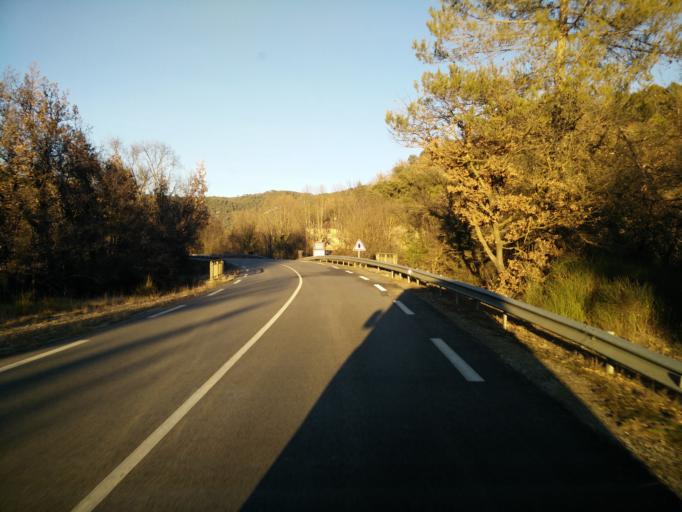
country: FR
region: Provence-Alpes-Cote d'Azur
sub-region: Departement du Var
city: Montferrat
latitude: 43.6024
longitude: 6.4778
